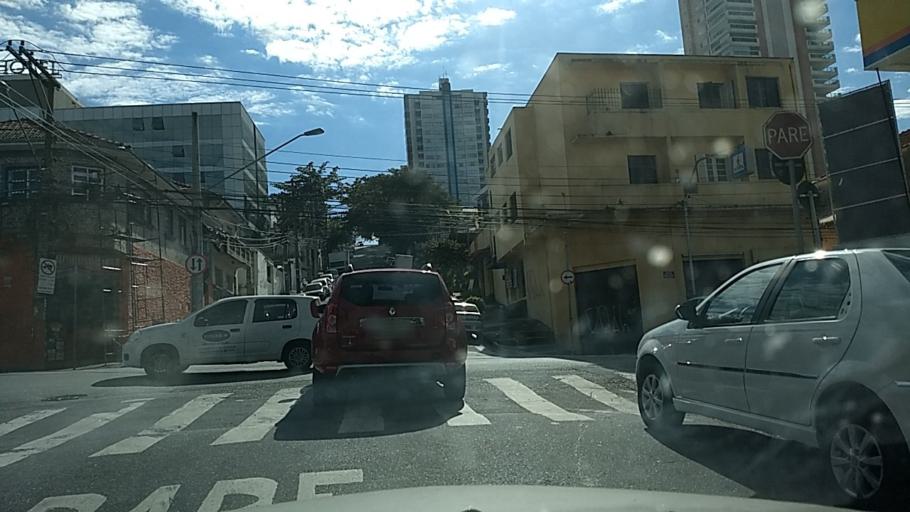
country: BR
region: Sao Paulo
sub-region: Sao Paulo
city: Sao Paulo
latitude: -23.5062
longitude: -46.6035
